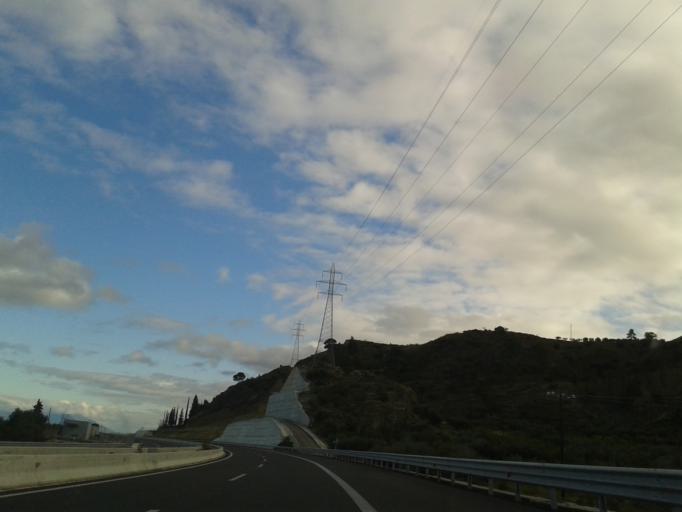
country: GR
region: Peloponnese
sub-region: Nomos Korinthias
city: Xylokastro
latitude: 38.0952
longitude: 22.5629
